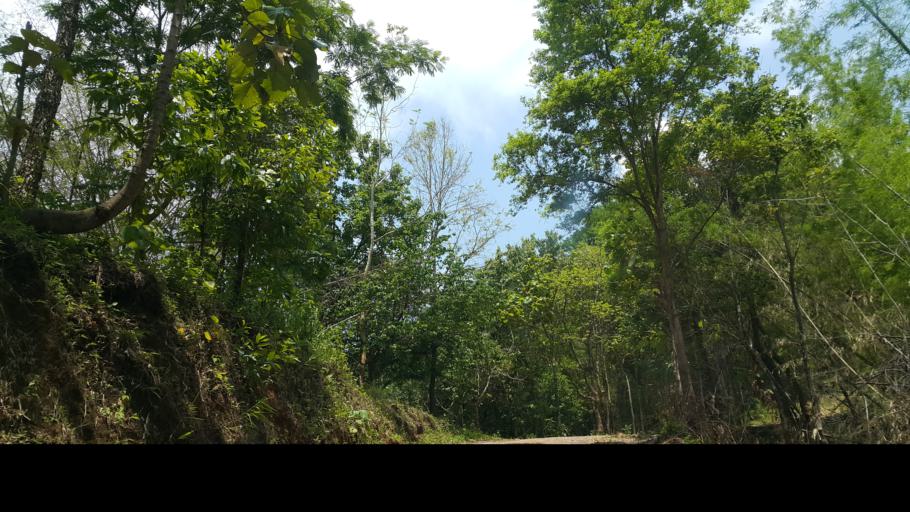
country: TH
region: Chiang Rai
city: Chiang Rai
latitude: 19.9986
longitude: 99.7096
